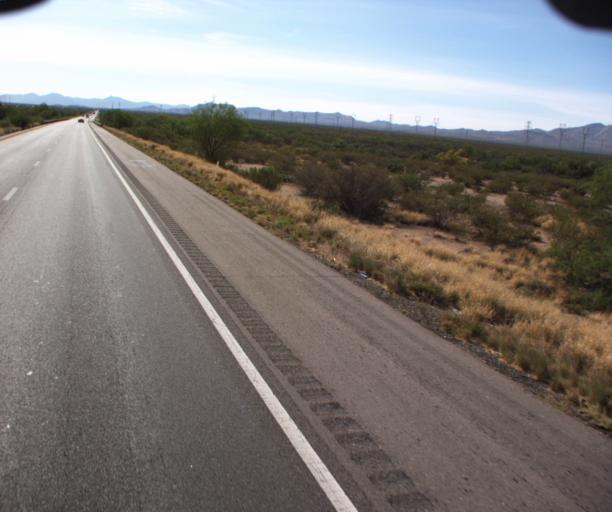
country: US
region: Arizona
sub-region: Pima County
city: Vail
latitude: 32.0465
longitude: -110.7500
